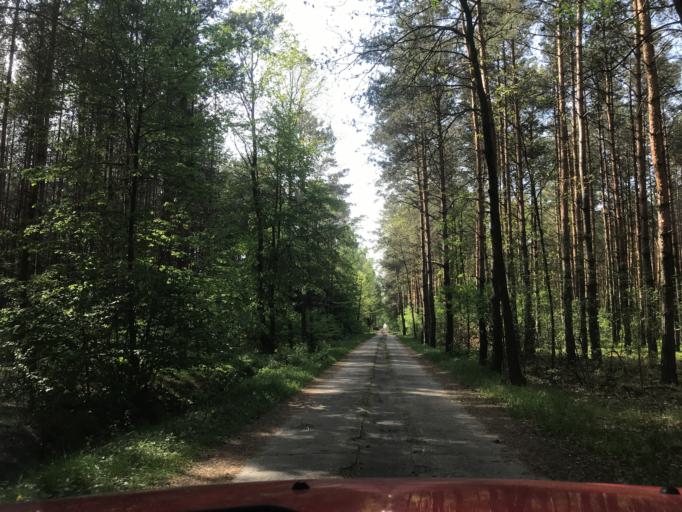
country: PL
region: Greater Poland Voivodeship
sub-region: Powiat kaliski
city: Stawiszyn
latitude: 51.9390
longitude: 18.1607
